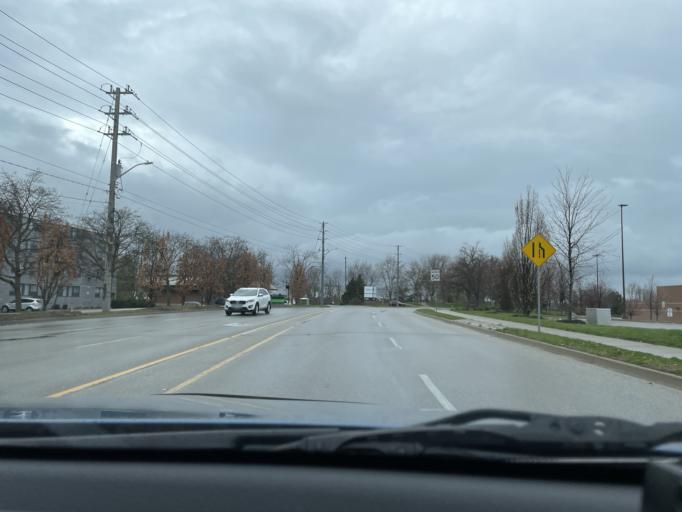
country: CA
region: Ontario
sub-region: Wellington County
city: Guelph
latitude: 43.5159
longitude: -80.2399
